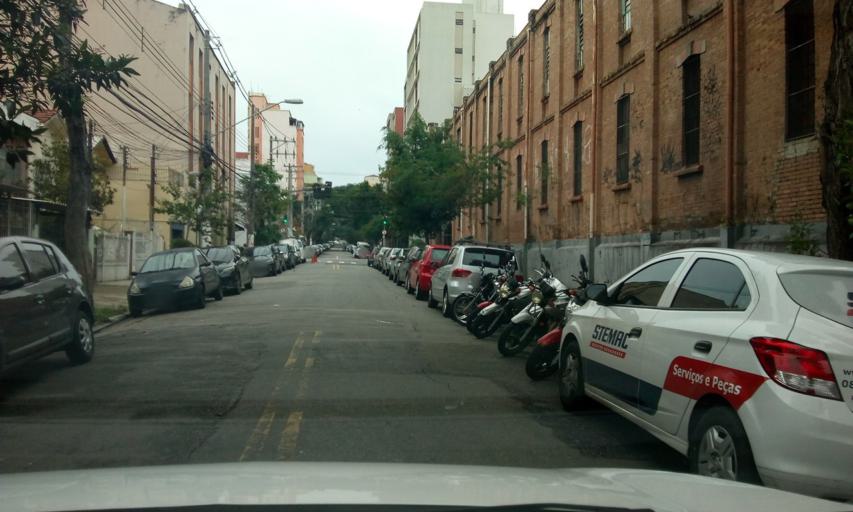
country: BR
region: Sao Paulo
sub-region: Sao Paulo
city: Sao Paulo
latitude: -23.5301
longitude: -46.6497
